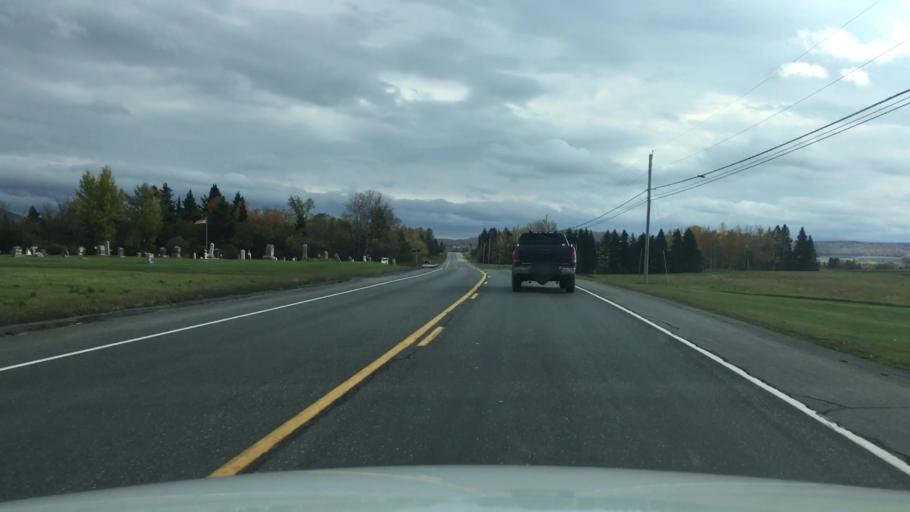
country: US
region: Maine
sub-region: Aroostook County
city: Easton
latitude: 46.5643
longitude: -67.9474
